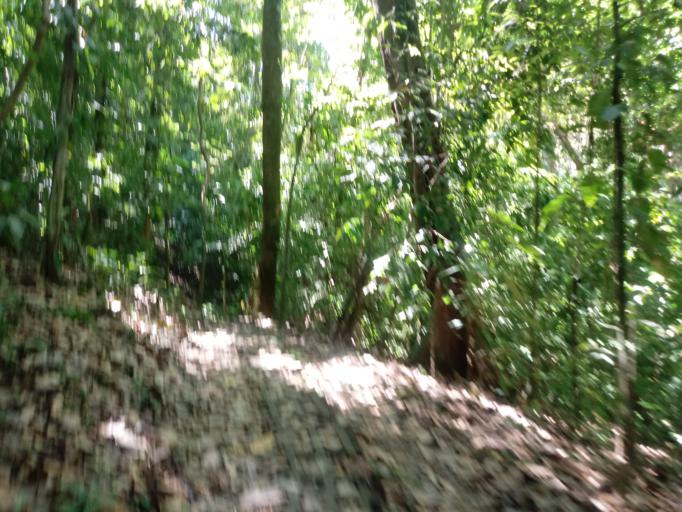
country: CR
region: Puntarenas
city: Paquera
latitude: 9.5855
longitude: -85.0994
